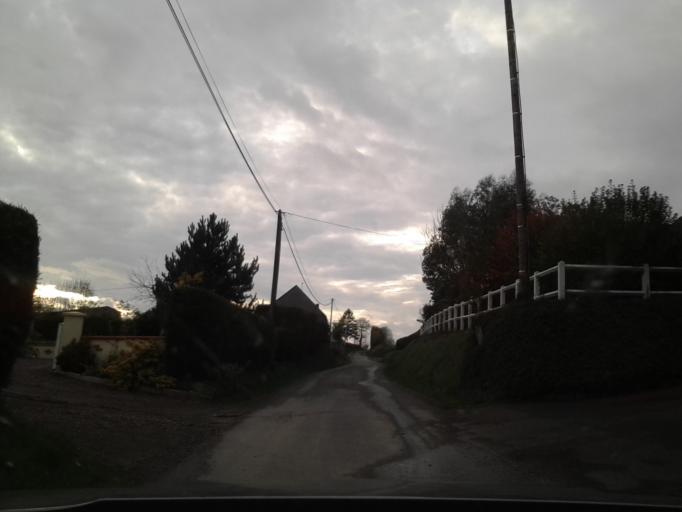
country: FR
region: Lower Normandy
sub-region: Departement du Calvados
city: Vassy
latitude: 48.8788
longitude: -0.6868
